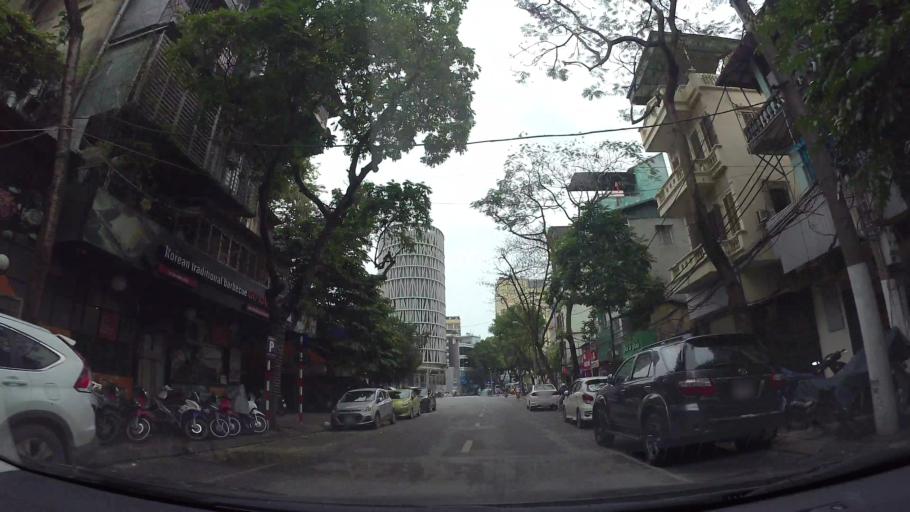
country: VN
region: Ha Noi
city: Hai BaTrung
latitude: 21.0183
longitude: 105.8577
